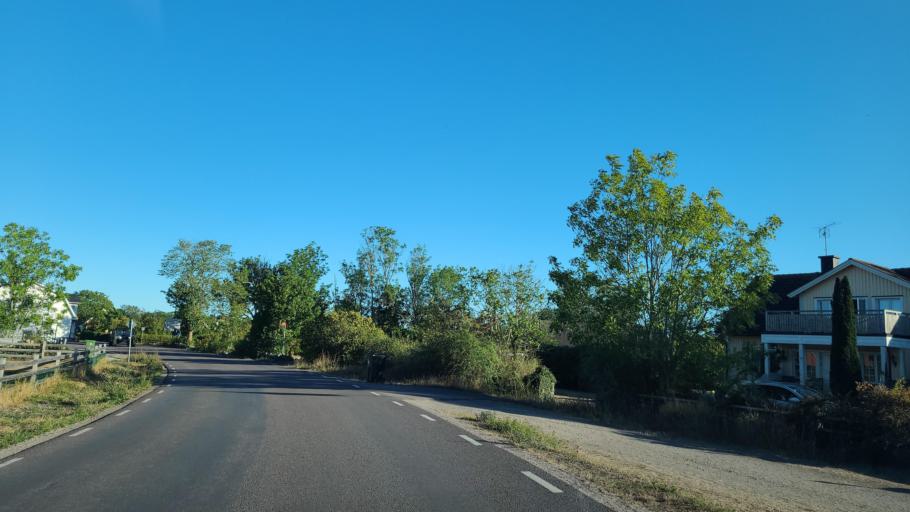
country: SE
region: Kalmar
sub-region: Borgholms Kommun
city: Borgholm
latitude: 57.3182
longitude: 17.0164
